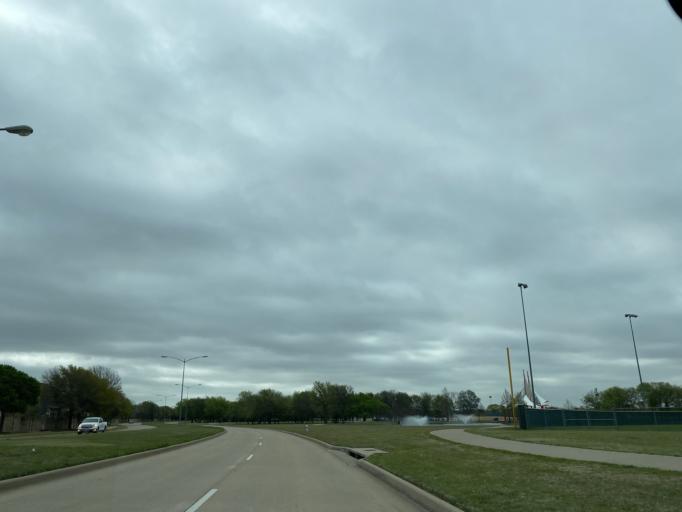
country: US
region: Texas
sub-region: Collin County
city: Allen
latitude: 33.1102
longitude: -96.6261
